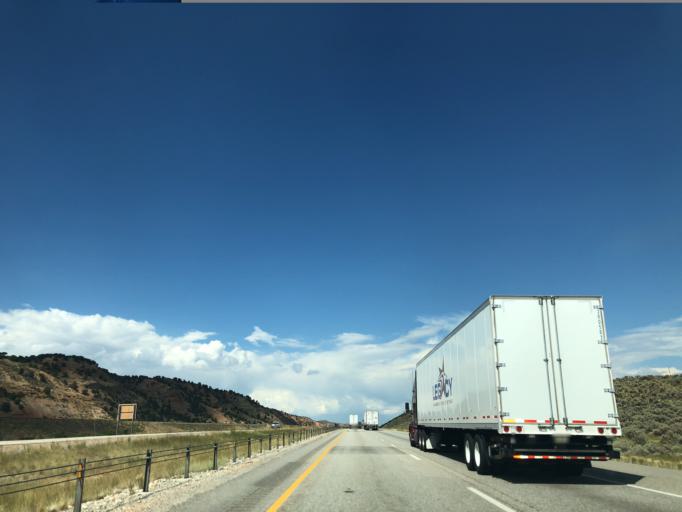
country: US
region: Utah
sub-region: Summit County
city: Coalville
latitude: 41.0934
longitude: -111.2219
